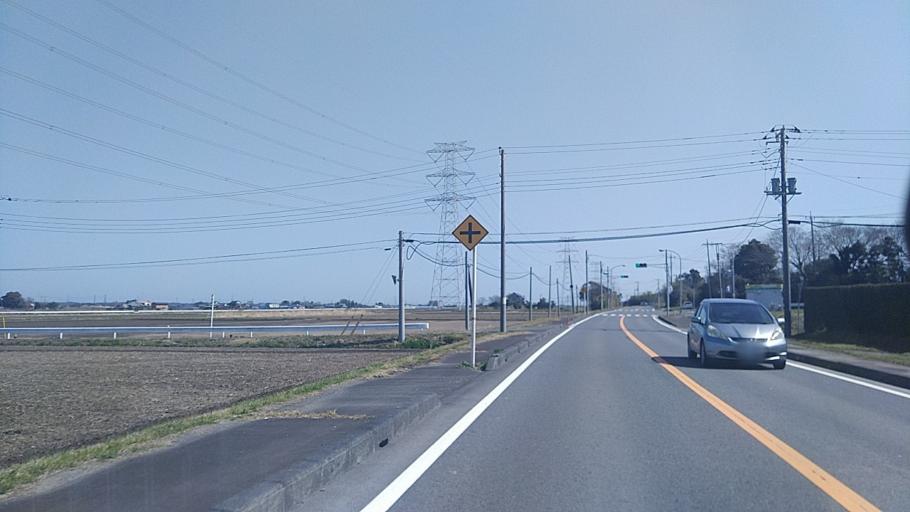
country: JP
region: Ibaraki
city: Edosaki
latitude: 35.8800
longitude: 140.3158
